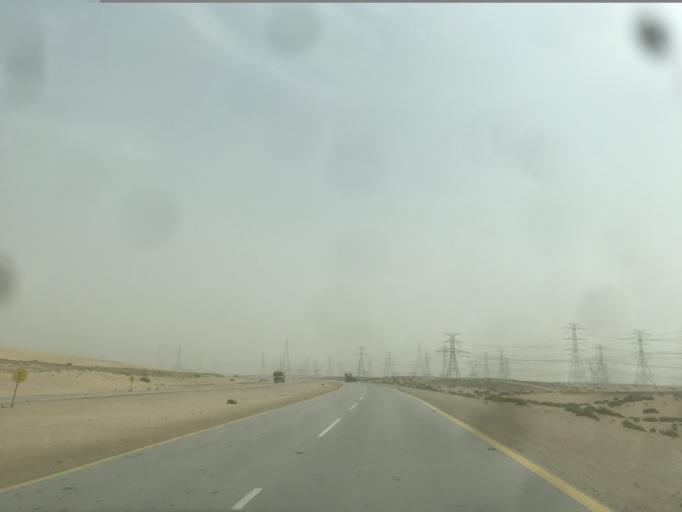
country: SA
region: Eastern Province
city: Abqaiq
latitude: 25.9080
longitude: 49.8884
